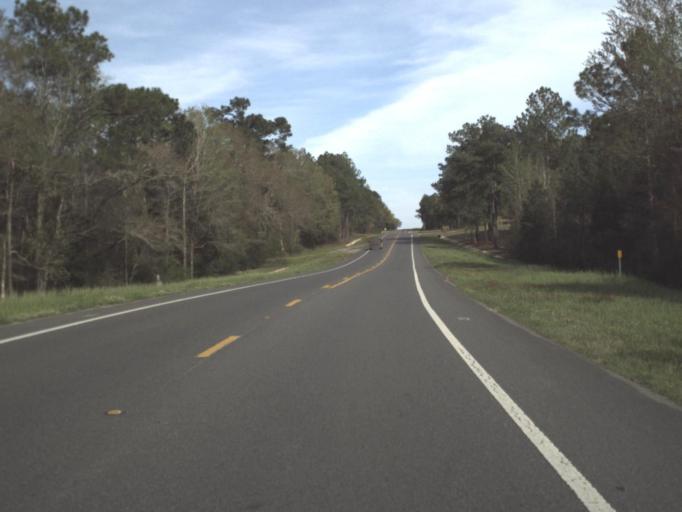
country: US
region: Florida
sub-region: Holmes County
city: Bonifay
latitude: 30.7947
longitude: -85.7241
